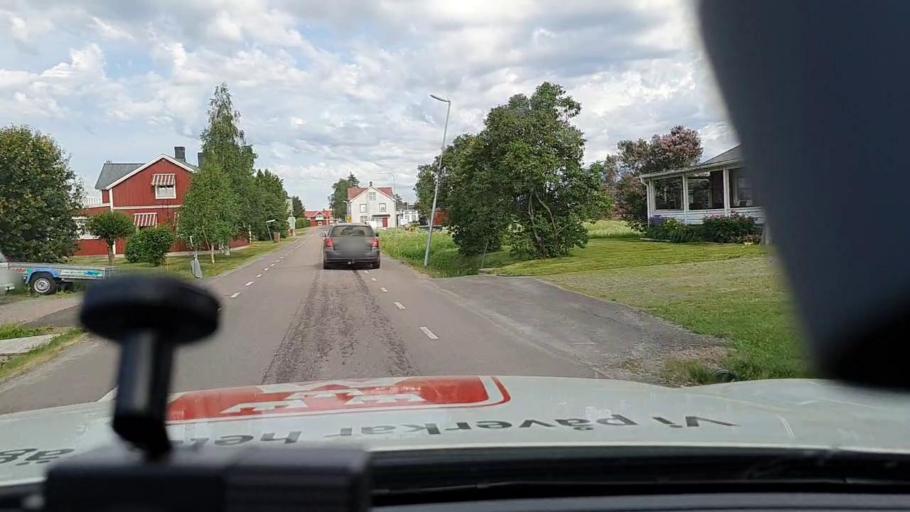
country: SE
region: Norrbotten
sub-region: Bodens Kommun
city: Saevast
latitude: 65.6792
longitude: 21.8072
